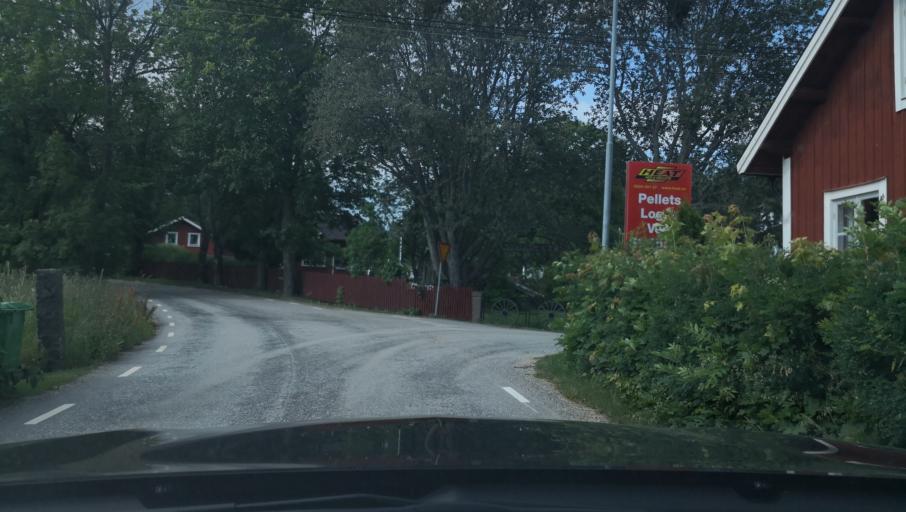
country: SE
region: Vaestmanland
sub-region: Norbergs Kommun
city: Norberg
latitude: 59.9809
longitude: 15.9580
